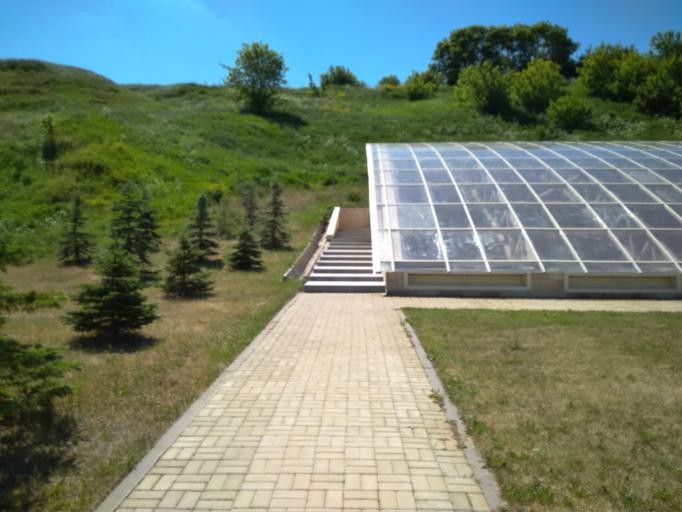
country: RU
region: Tatarstan
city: Bolgar
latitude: 54.9868
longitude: 49.0503
